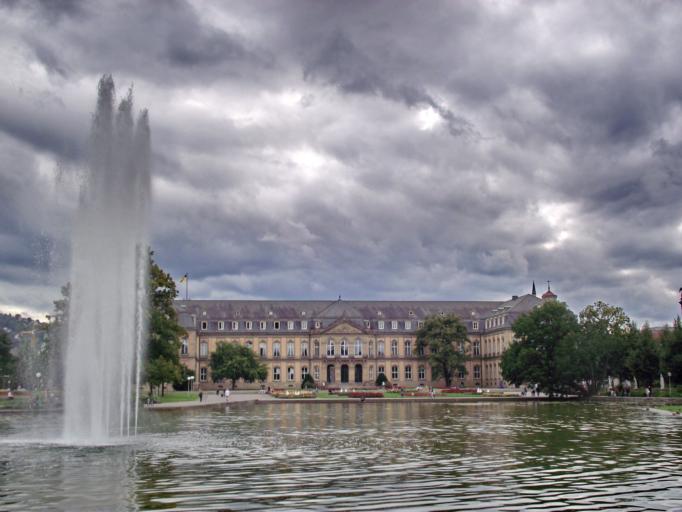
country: DE
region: Baden-Wuerttemberg
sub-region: Regierungsbezirk Stuttgart
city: Stuttgart
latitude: 48.7804
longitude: 9.1834
